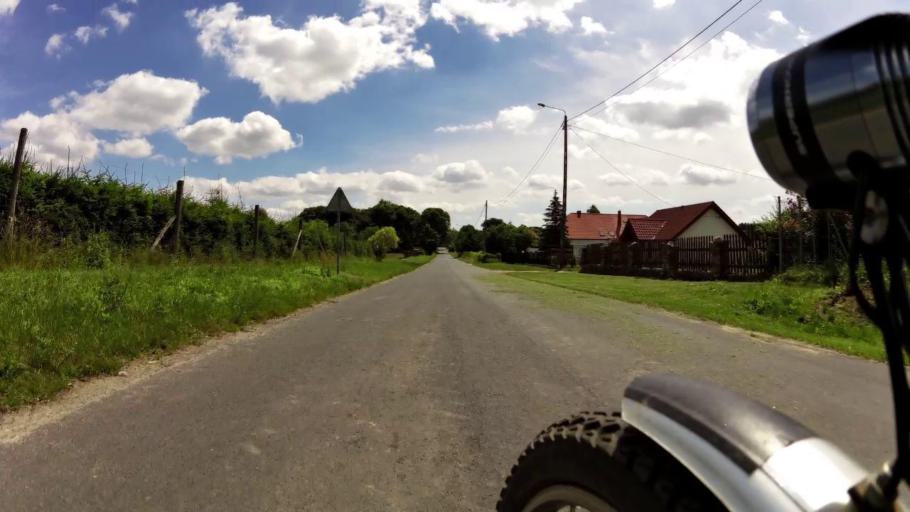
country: PL
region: West Pomeranian Voivodeship
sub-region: Powiat choszczenski
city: Choszczno
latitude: 53.2235
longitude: 15.4294
